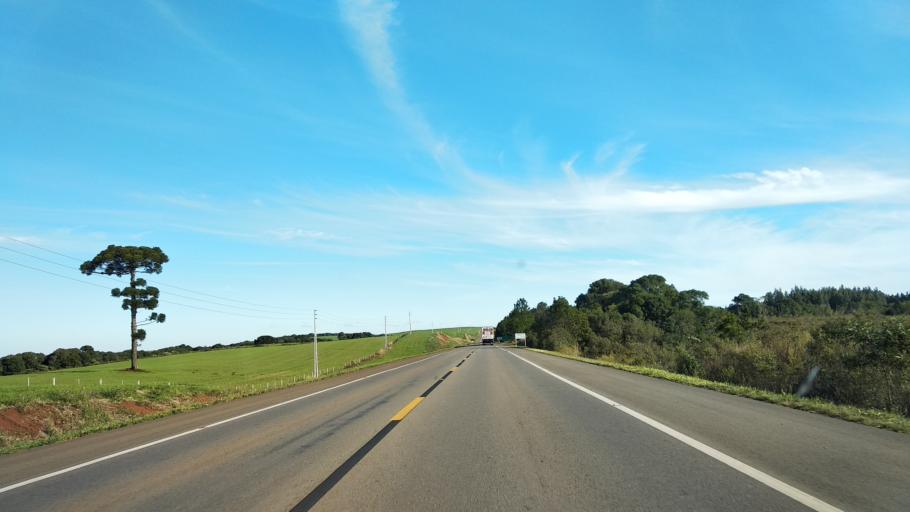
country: BR
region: Santa Catarina
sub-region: Celso Ramos
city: Celso Ramos
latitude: -27.5080
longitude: -51.3458
